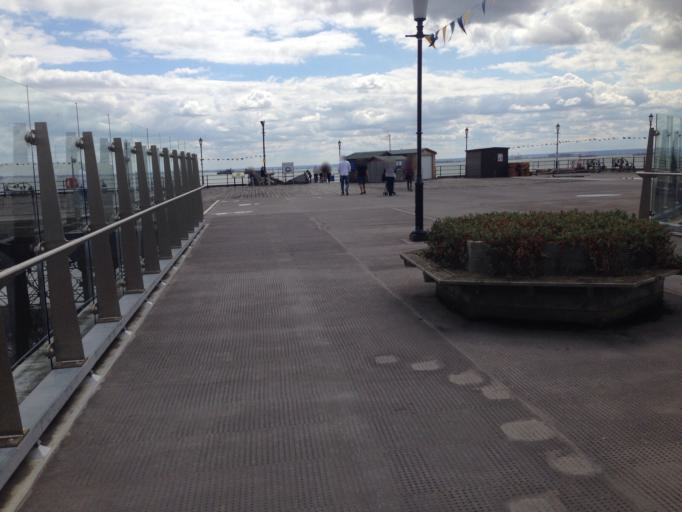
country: GB
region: England
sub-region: Southend-on-Sea
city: Southend-on-Sea
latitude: 51.5322
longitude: 0.7161
